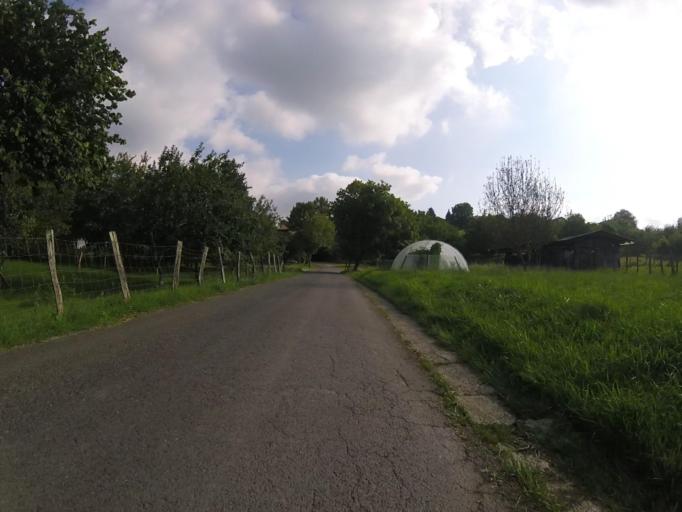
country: ES
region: Basque Country
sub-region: Provincia de Guipuzcoa
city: Astigarraga
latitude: 43.2576
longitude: -1.9501
